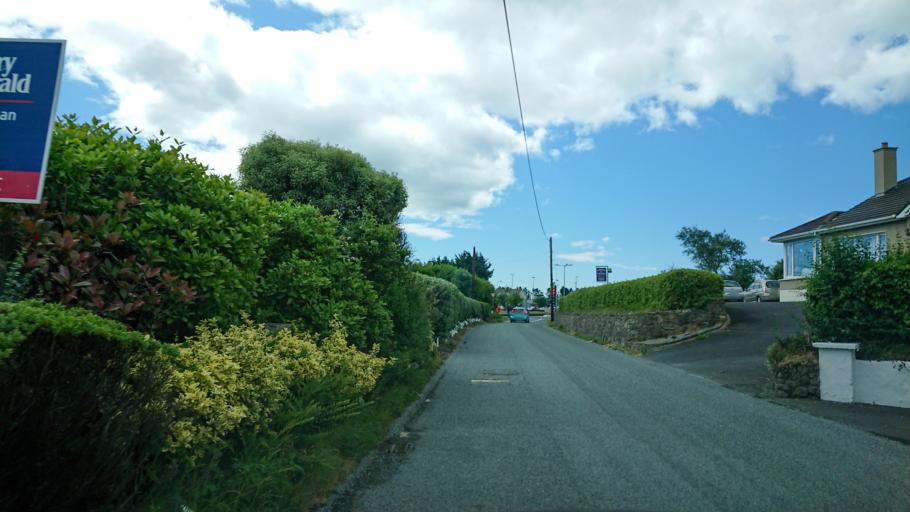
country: IE
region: Munster
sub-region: Waterford
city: Tra Mhor
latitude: 52.1738
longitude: -7.1403
